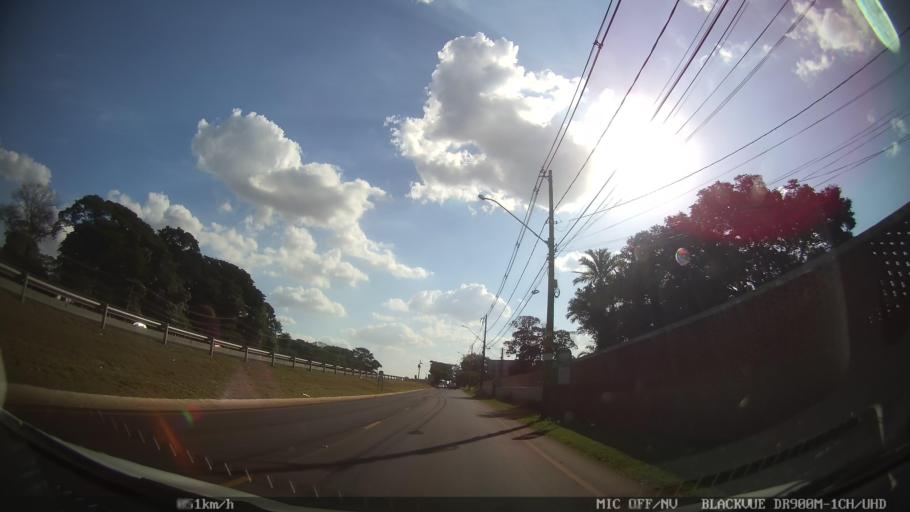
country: BR
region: Sao Paulo
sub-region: Ribeirao Preto
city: Ribeirao Preto
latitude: -21.1774
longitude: -47.8430
